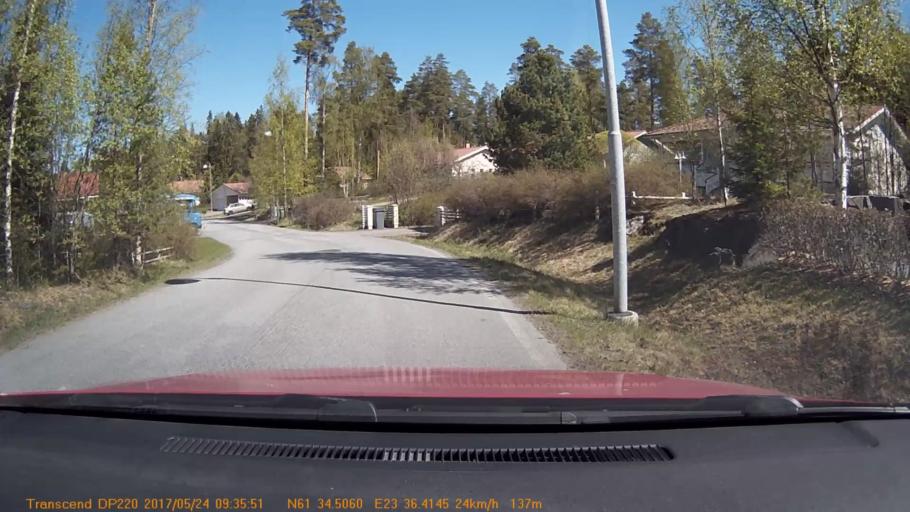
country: FI
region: Pirkanmaa
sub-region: Tampere
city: Yloejaervi
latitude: 61.5753
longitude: 23.6073
